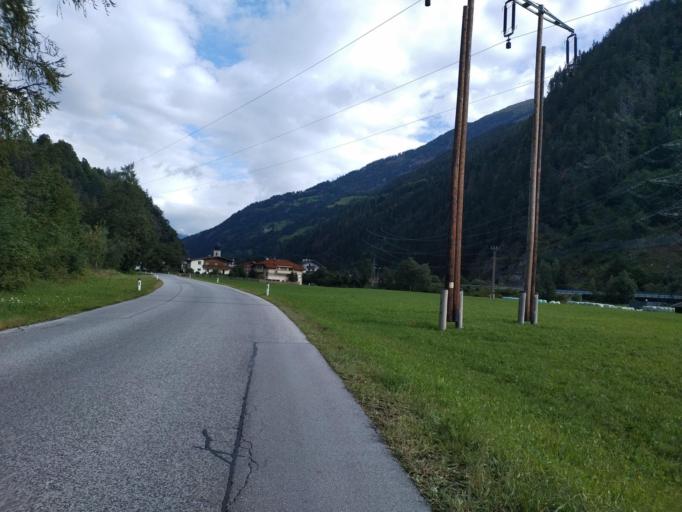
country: AT
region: Tyrol
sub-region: Politischer Bezirk Lienz
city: Hopfgarten in Defereggen
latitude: 46.9317
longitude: 12.5752
